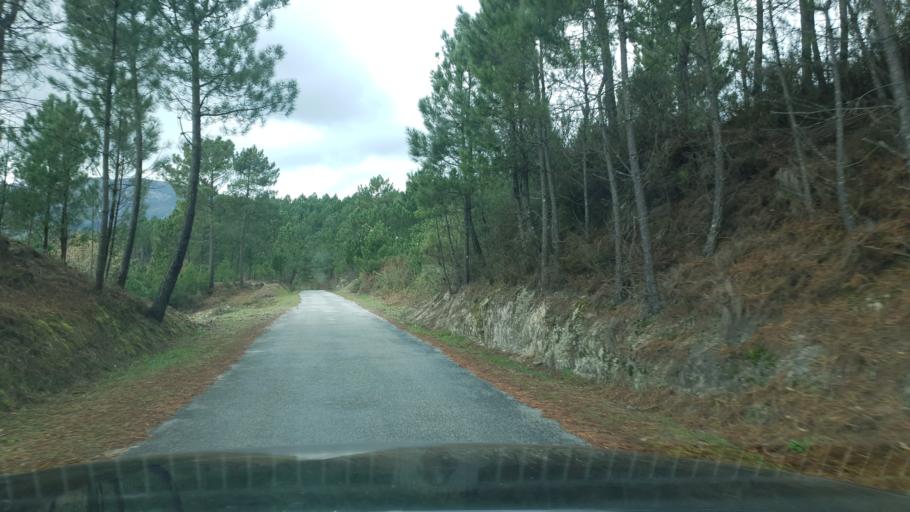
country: PT
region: Viseu
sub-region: Castro Daire
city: Castro Daire
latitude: 40.8807
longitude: -8.0057
